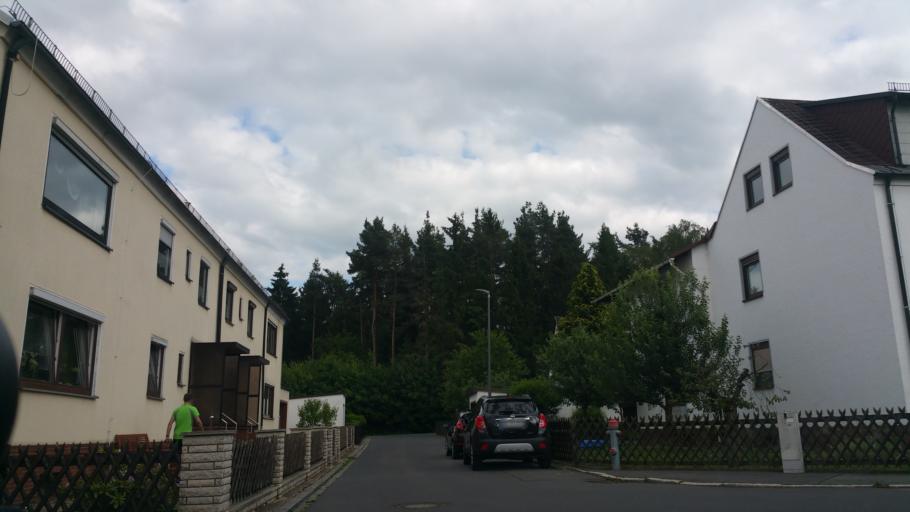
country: DE
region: Bavaria
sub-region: Upper Franconia
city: Rehau
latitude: 50.2366
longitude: 12.0207
